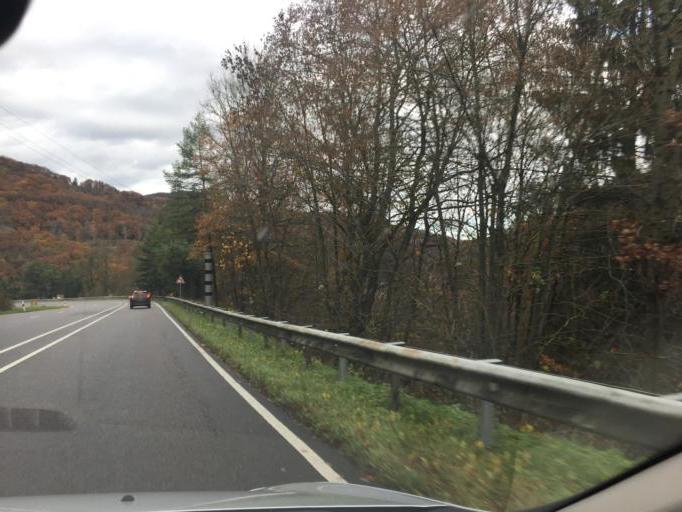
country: LU
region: Diekirch
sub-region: Canton de Wiltz
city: Goesdorf
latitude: 49.9032
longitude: 5.9597
